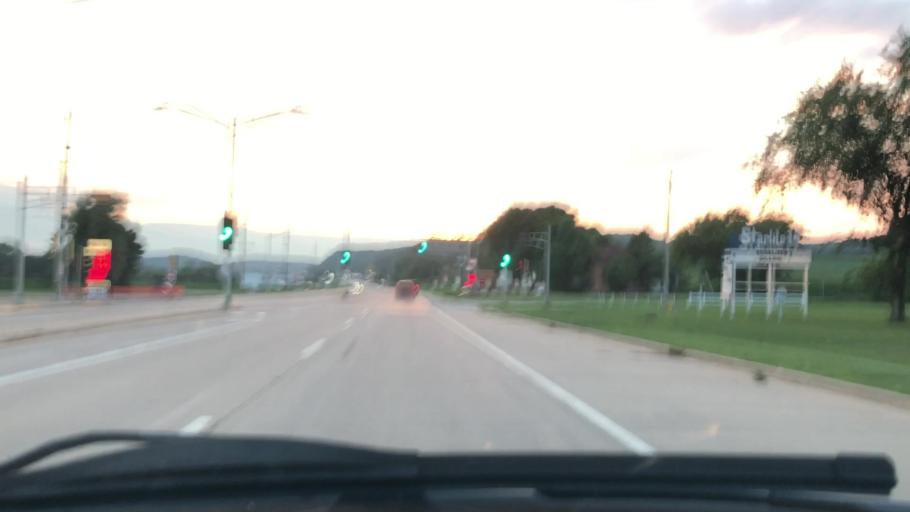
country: US
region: Wisconsin
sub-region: Richland County
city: Richland Center
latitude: 43.3152
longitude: -90.3497
